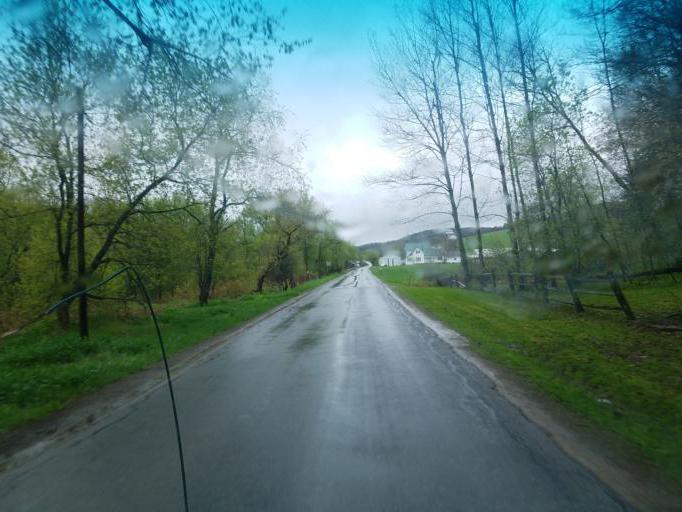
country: US
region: Pennsylvania
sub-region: Tioga County
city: Westfield
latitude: 41.9553
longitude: -77.6477
